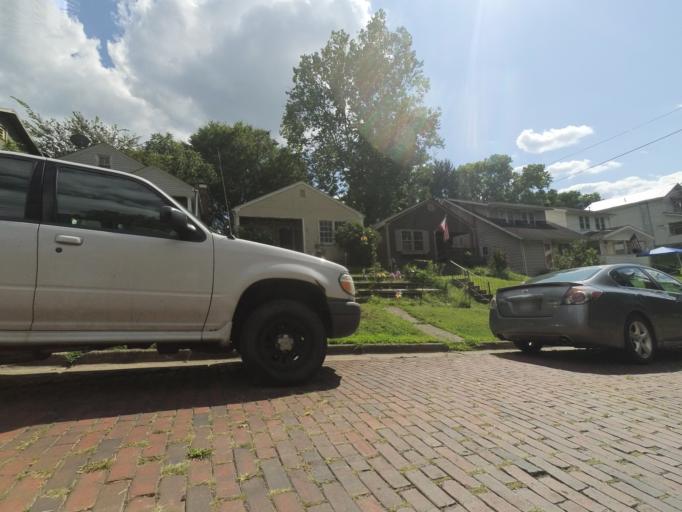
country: US
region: West Virginia
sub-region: Cabell County
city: Huntington
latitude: 38.4070
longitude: -82.4188
